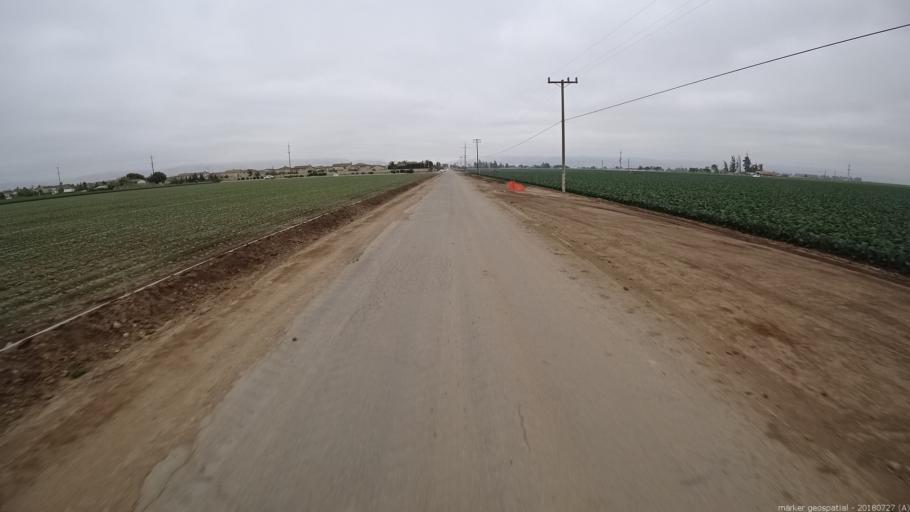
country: US
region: California
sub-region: Monterey County
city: Greenfield
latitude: 36.3371
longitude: -121.2300
